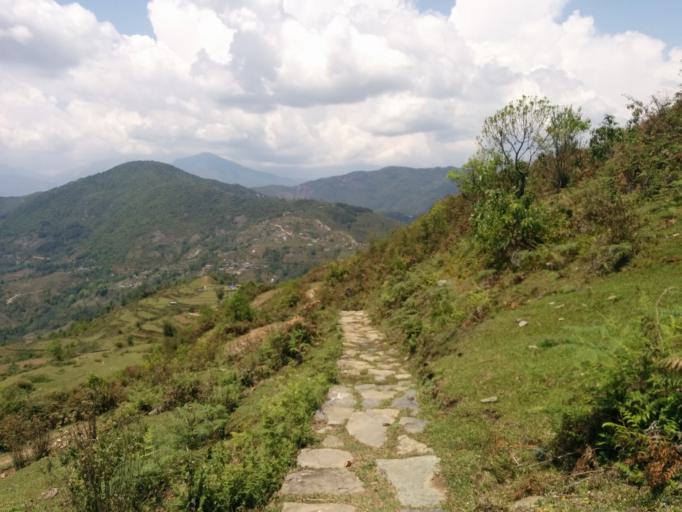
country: NP
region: Western Region
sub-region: Gandaki Zone
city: Pokhara
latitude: 28.2559
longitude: 83.8224
